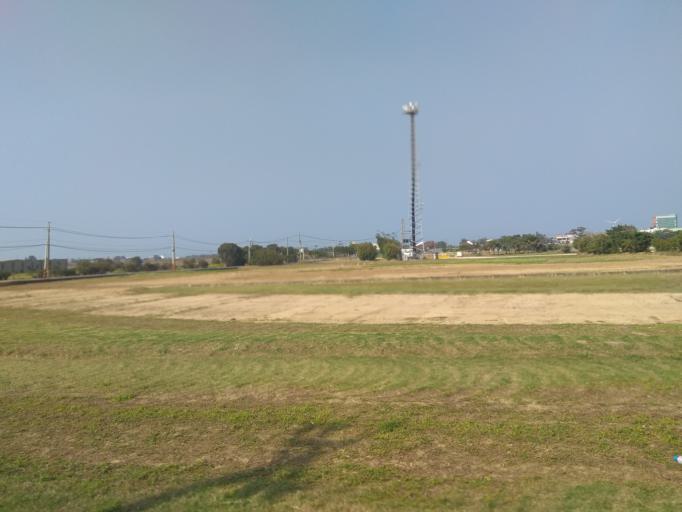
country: TW
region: Taiwan
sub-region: Hsinchu
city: Zhubei
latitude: 25.0038
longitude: 121.0479
